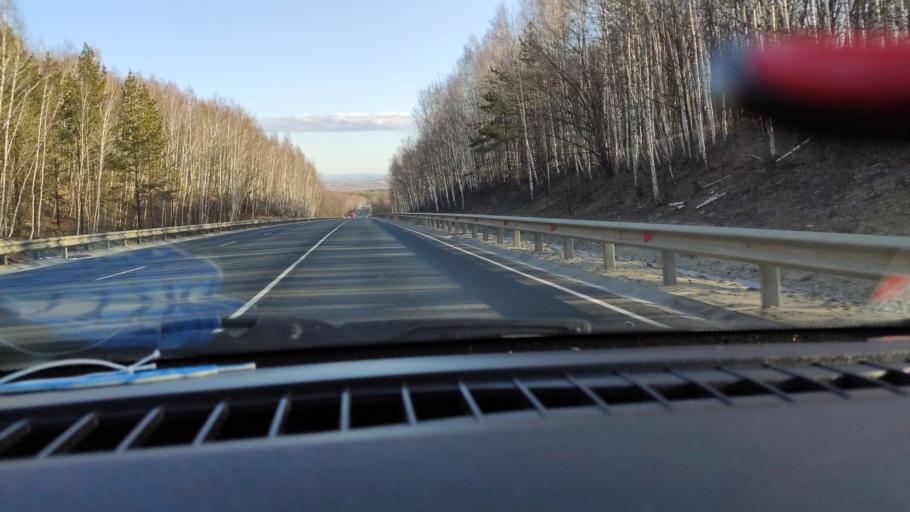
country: RU
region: Saratov
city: Khvalynsk
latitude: 52.5037
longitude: 48.0152
